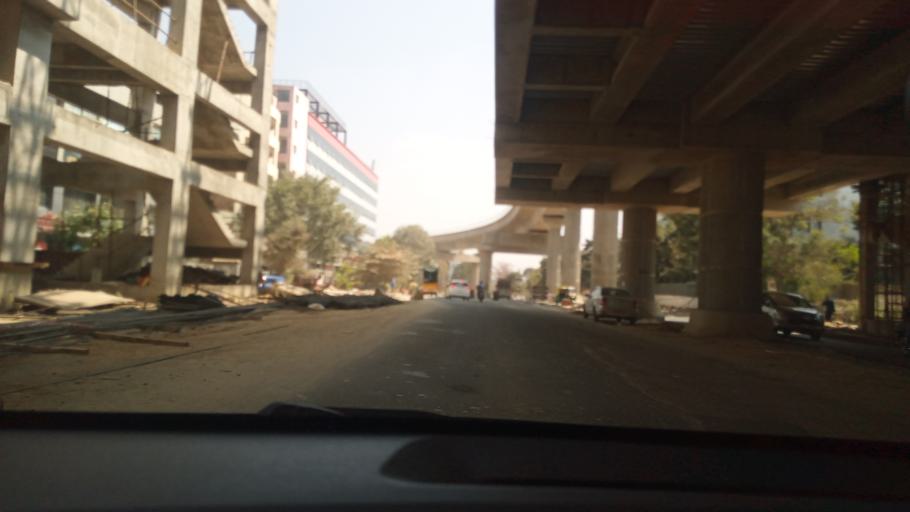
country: IN
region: Karnataka
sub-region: Bangalore Rural
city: Hoskote
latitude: 12.9766
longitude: 77.7251
